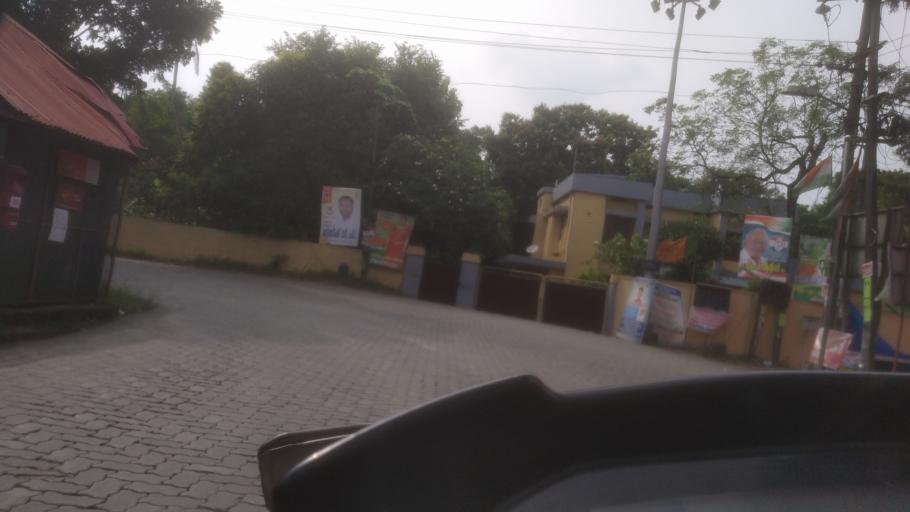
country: IN
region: Kerala
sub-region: Ernakulam
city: Angamali
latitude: 10.1659
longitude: 76.4110
